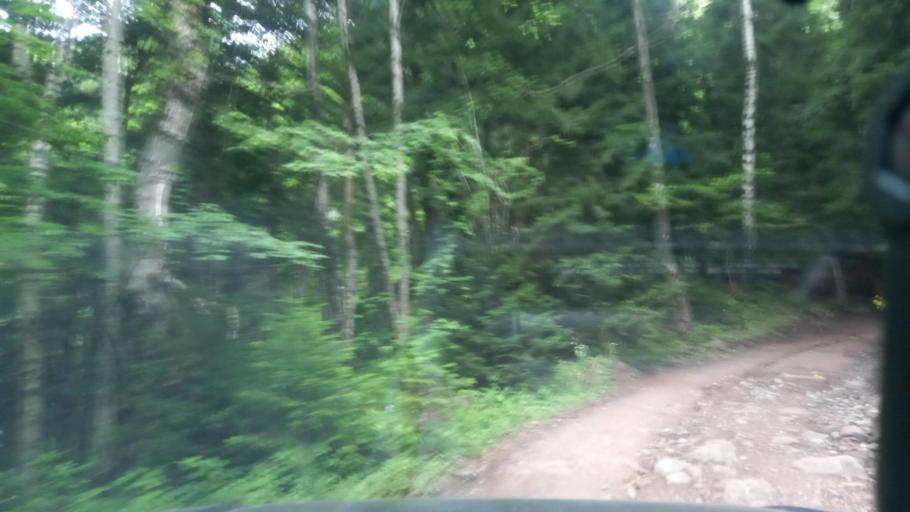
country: RU
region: Karachayevo-Cherkesiya
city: Kurdzhinovo
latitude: 43.8145
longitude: 40.8793
